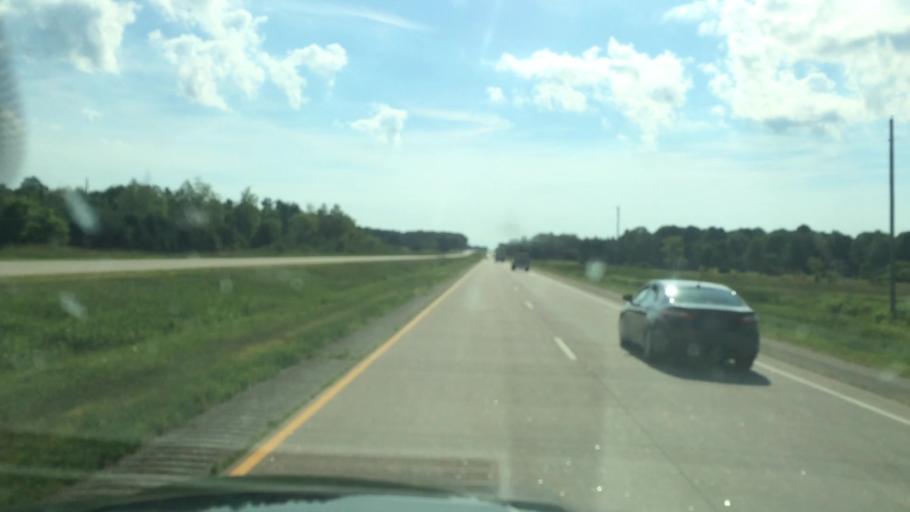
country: US
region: Wisconsin
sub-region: Waupaca County
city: Marion
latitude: 44.8039
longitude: -88.9956
